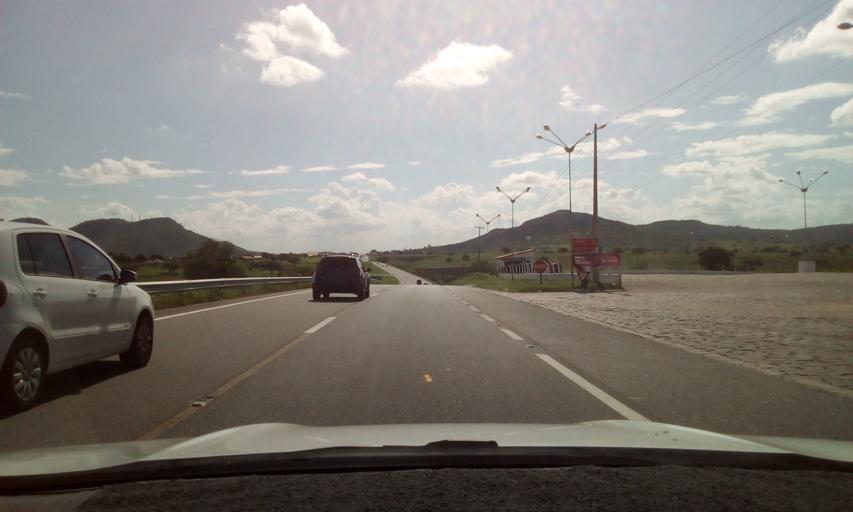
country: BR
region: Paraiba
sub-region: Gurinhem
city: Gurinhem
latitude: -7.1686
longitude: -35.3720
